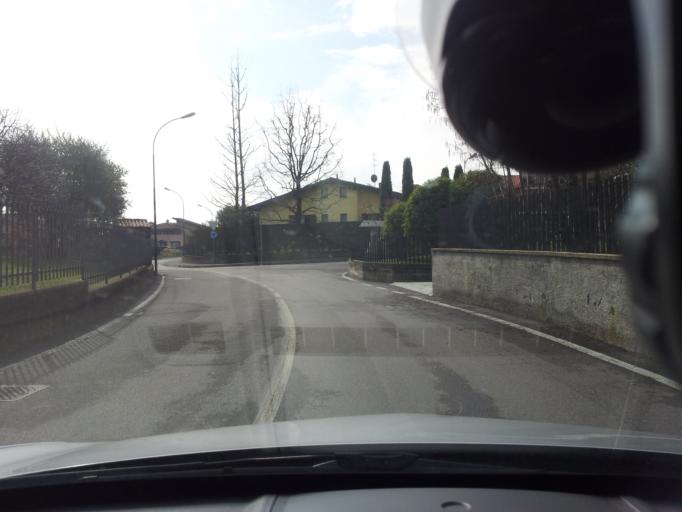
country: IT
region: Lombardy
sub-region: Provincia di Bergamo
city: Tagliuno
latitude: 45.6478
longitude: 9.9109
